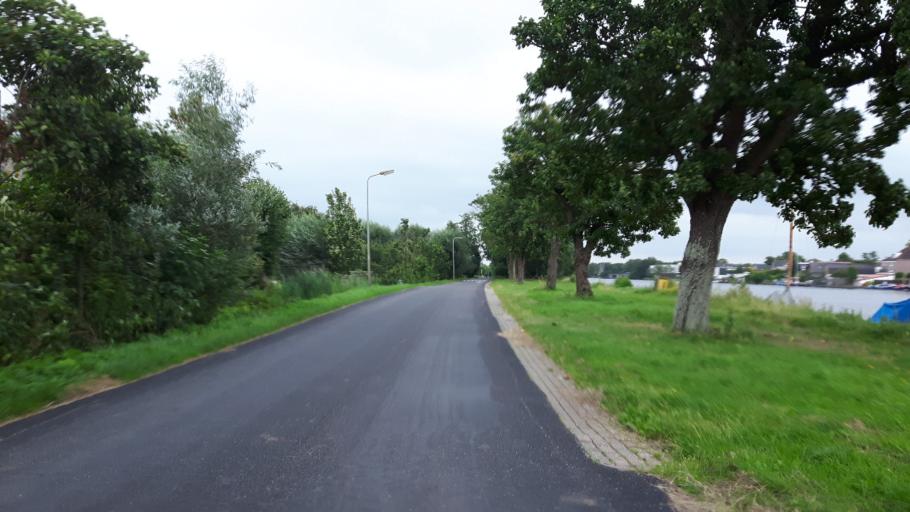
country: NL
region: South Holland
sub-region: Gemeente Alphen aan den Rijn
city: Alphen aan den Rijn
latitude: 52.1177
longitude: 4.6919
